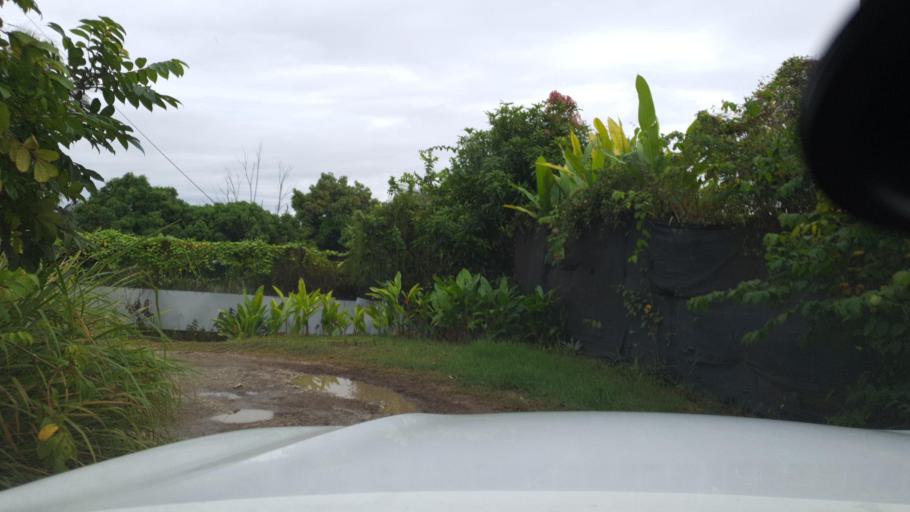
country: SB
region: Guadalcanal
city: Honiara
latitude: -9.4399
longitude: 159.9676
